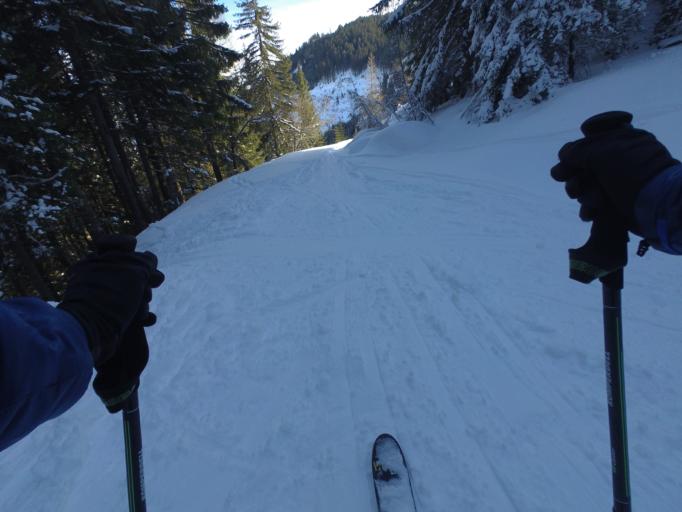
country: AT
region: Salzburg
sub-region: Politischer Bezirk Zell am See
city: Lend
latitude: 47.2781
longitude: 13.0135
